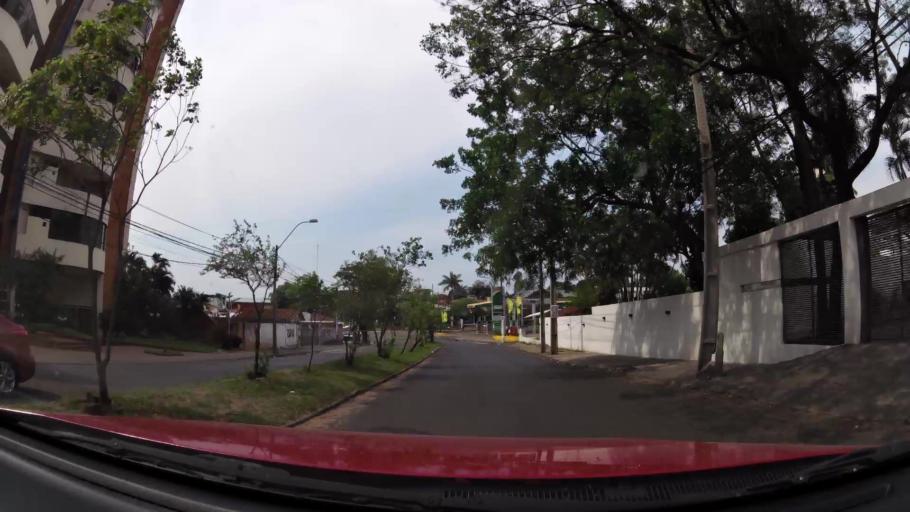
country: PY
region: Asuncion
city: Asuncion
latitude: -25.2765
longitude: -57.5677
